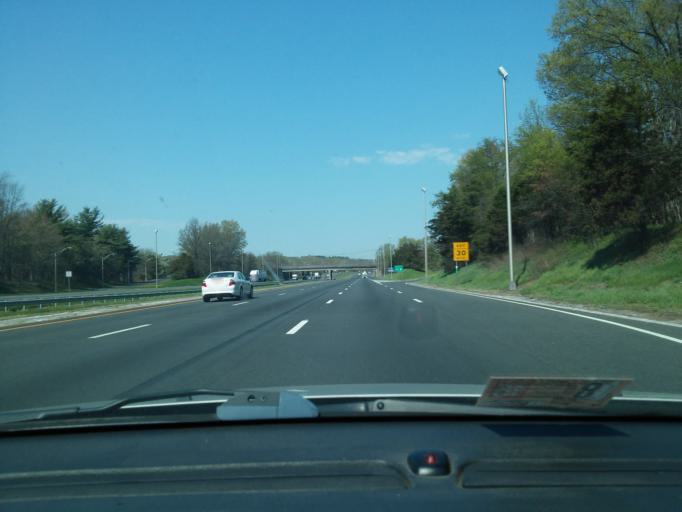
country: US
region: New Jersey
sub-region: Hunterdon County
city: Whitehouse Station
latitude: 40.6443
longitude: -74.7123
